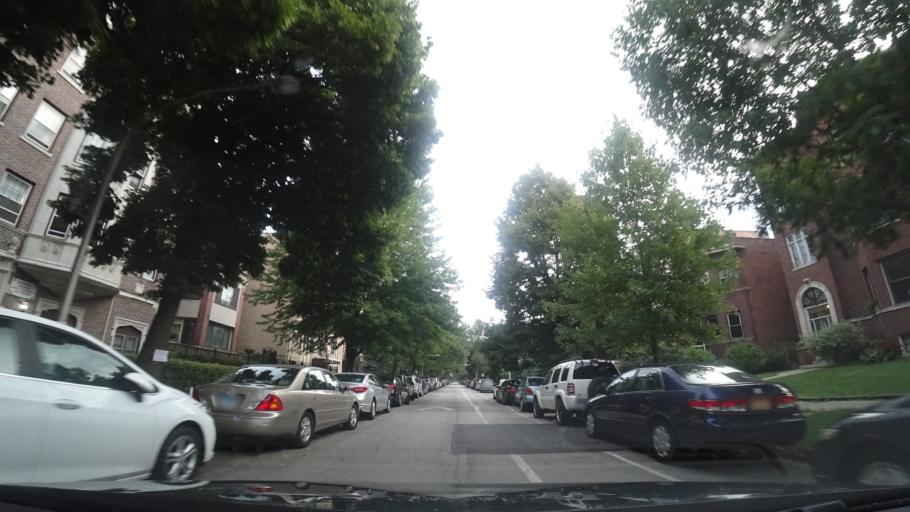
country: US
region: Illinois
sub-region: Cook County
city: Evanston
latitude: 41.9878
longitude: -87.6568
